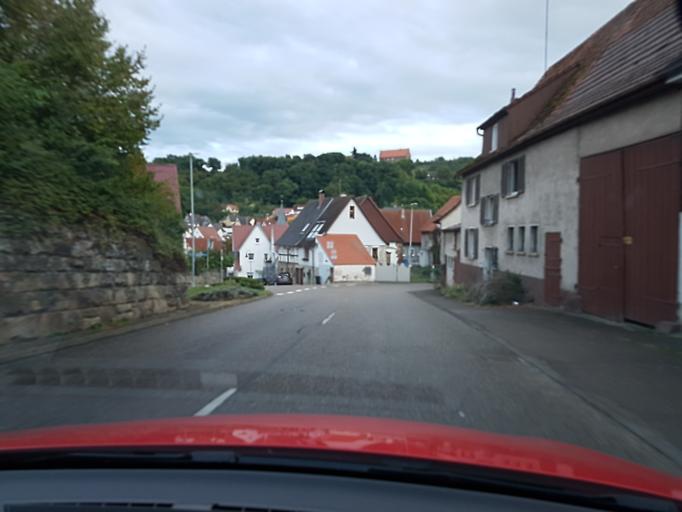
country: DE
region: Baden-Wuerttemberg
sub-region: Regierungsbezirk Stuttgart
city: Cleebronn
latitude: 49.0459
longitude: 9.0365
